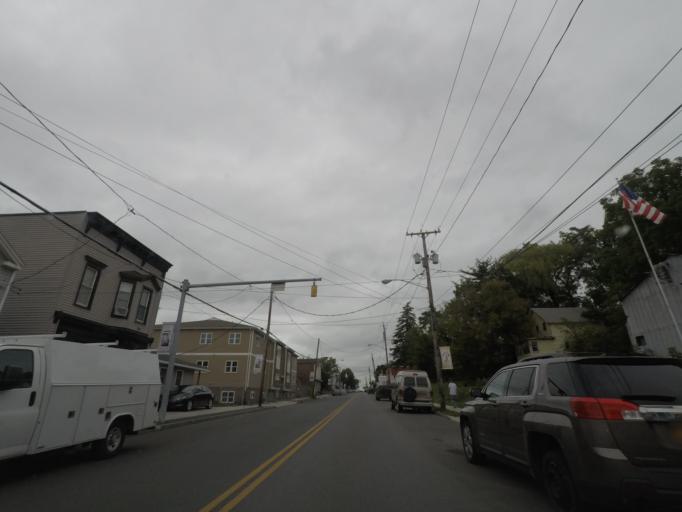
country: US
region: New York
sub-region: Rensselaer County
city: Rensselaer
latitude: 42.6486
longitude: -73.7385
